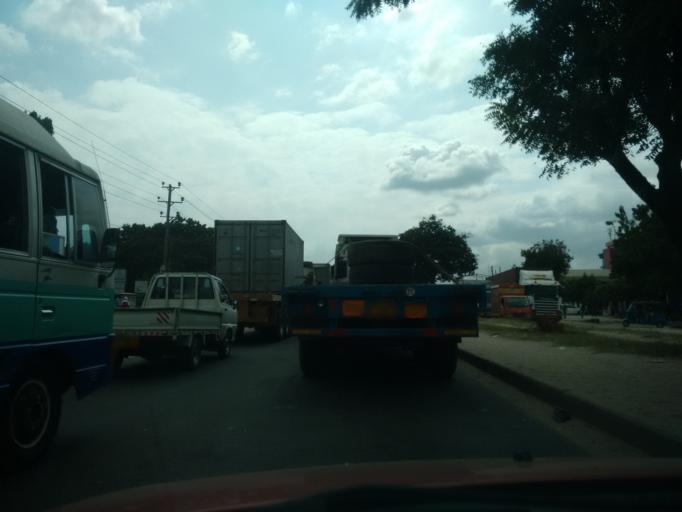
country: TZ
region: Dar es Salaam
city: Dar es Salaam
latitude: -6.8461
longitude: 39.2471
